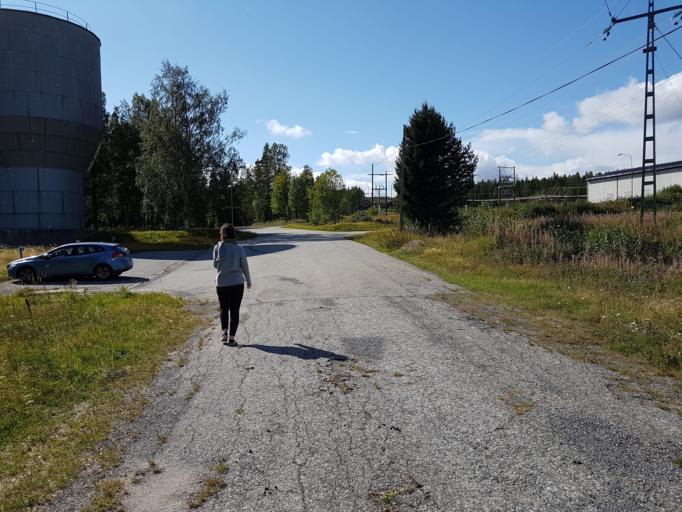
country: SE
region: Vaesternorrland
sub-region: OErnskoeldsviks Kommun
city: Husum
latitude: 63.3451
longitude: 19.1150
